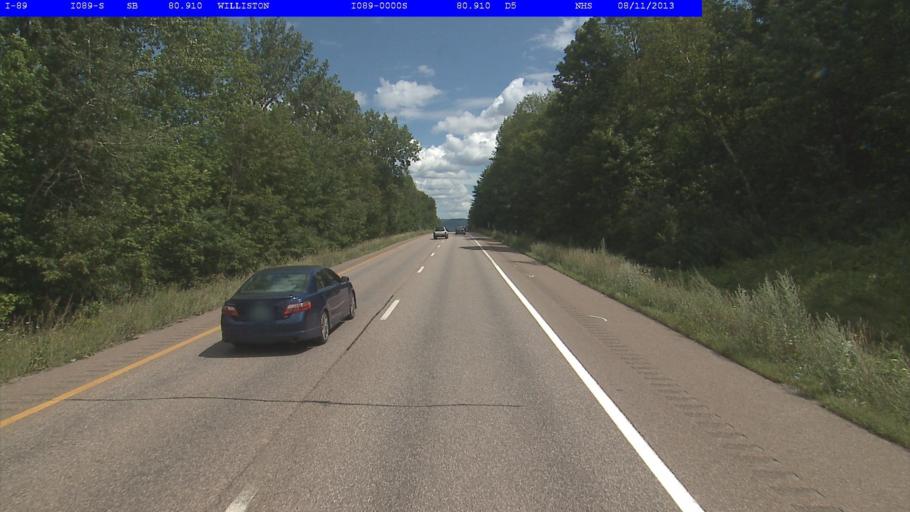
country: US
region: Vermont
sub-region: Chittenden County
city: Williston
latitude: 44.4330
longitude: -73.0544
